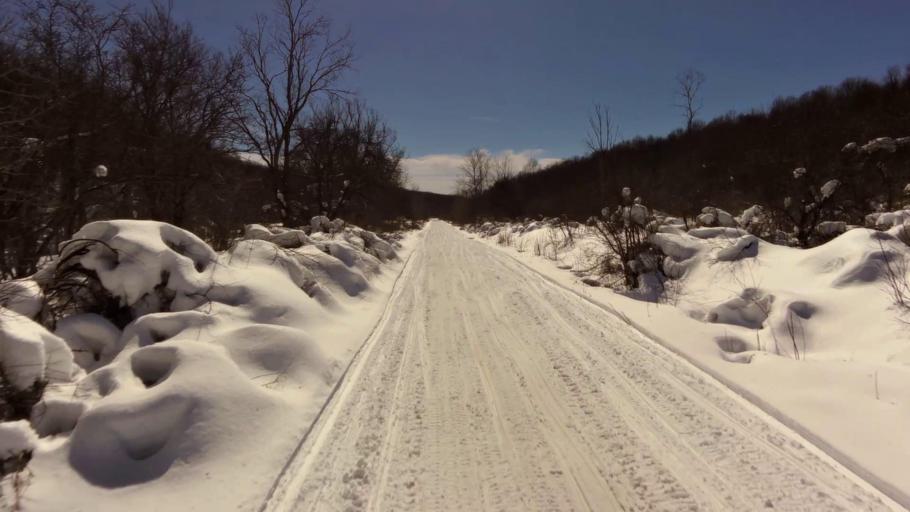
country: US
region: New York
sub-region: Cattaraugus County
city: Delevan
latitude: 42.4232
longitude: -78.4569
